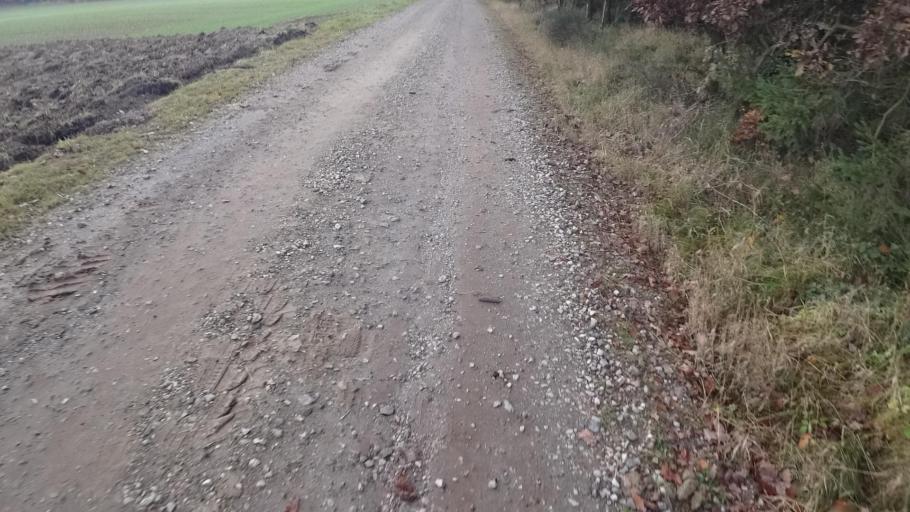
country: DE
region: Rheinland-Pfalz
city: Bickenbach
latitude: 50.1142
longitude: 7.5350
